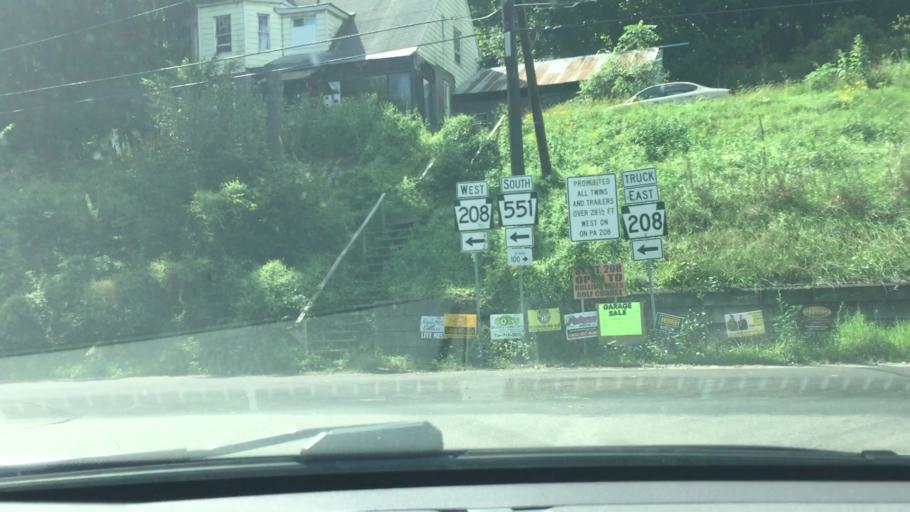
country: US
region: Pennsylvania
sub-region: Lawrence County
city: New Wilmington
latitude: 41.1132
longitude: -80.4378
